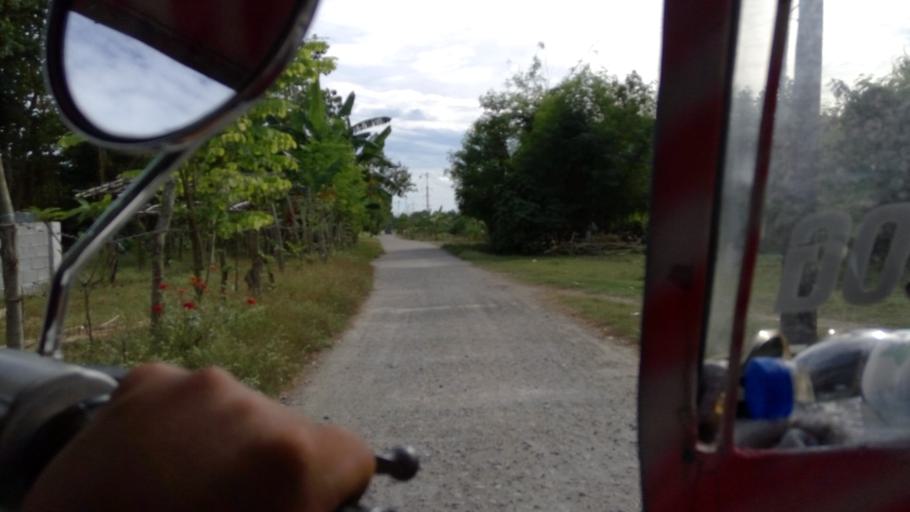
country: PH
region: Ilocos
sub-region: Province of La Union
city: San Eugenio
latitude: 16.3709
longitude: 120.3524
